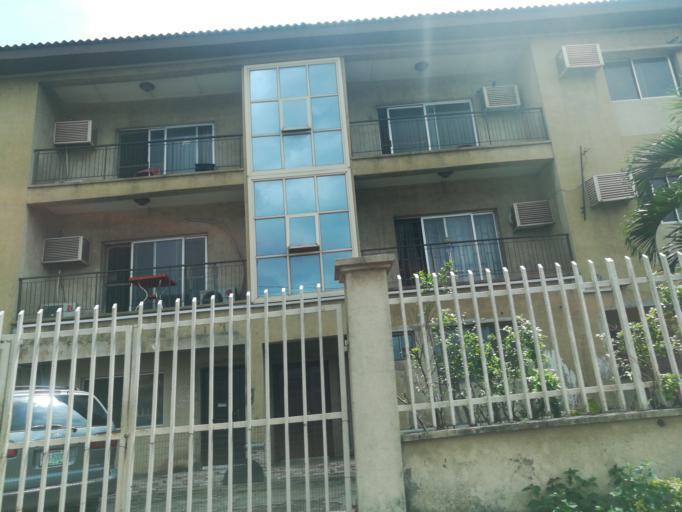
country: NG
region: Lagos
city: Mushin
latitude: 6.5276
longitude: 3.3657
